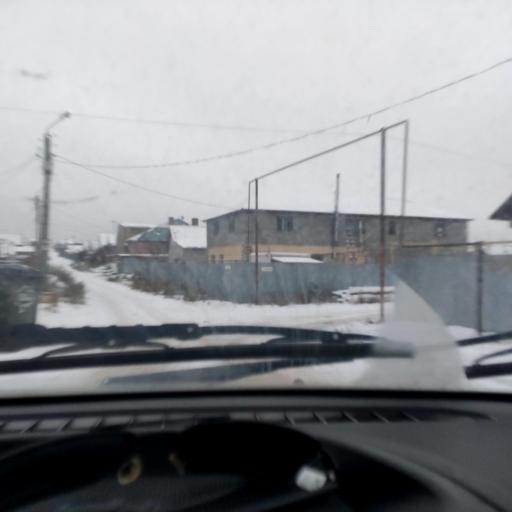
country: RU
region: Samara
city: Zhigulevsk
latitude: 53.4896
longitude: 49.5296
